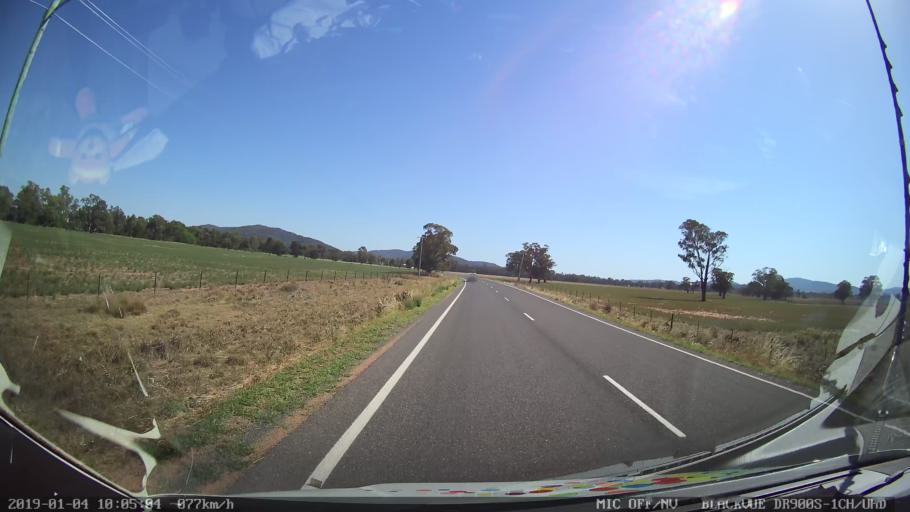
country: AU
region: New South Wales
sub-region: Cabonne
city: Canowindra
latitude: -33.4459
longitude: 148.3638
